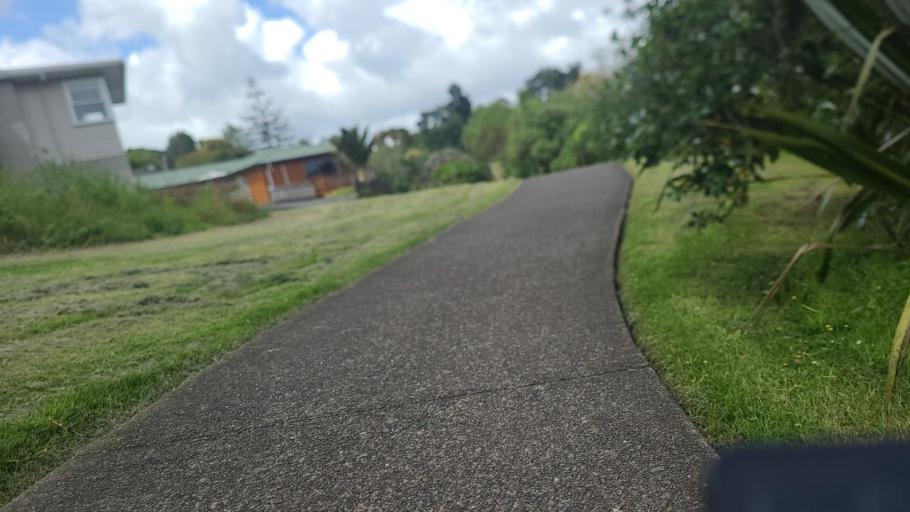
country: NZ
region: Auckland
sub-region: Auckland
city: Rosebank
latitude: -36.8568
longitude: 174.6407
